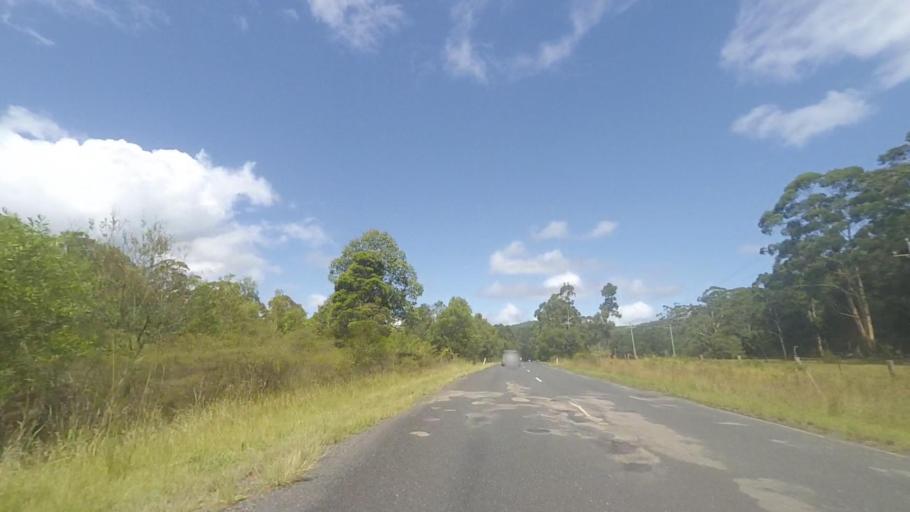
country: AU
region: New South Wales
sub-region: Great Lakes
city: Bulahdelah
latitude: -32.4021
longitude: 152.2691
